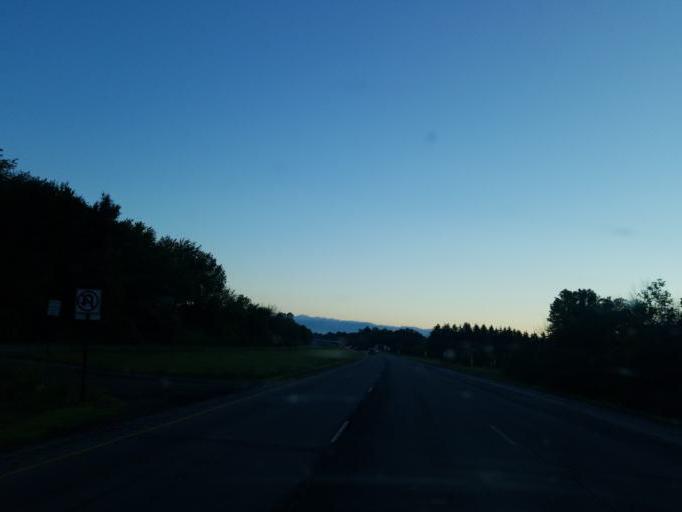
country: US
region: Ohio
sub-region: Summit County
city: Norton
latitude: 40.9977
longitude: -81.6617
